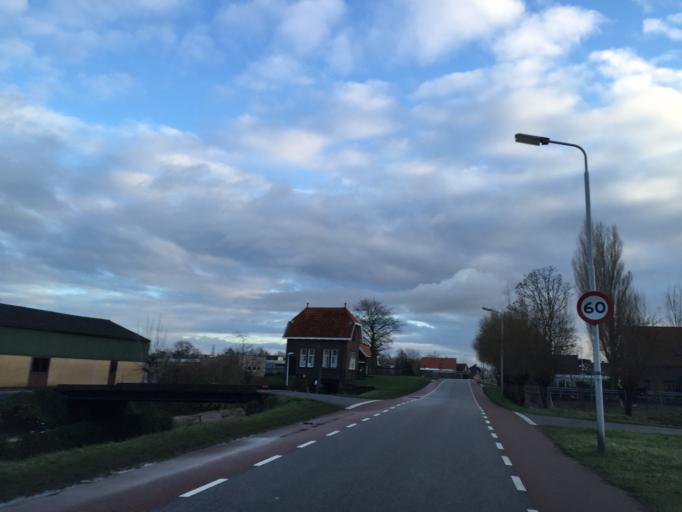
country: NL
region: South Holland
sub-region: Gemeente Pijnacker-Nootdorp
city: Pijnacker
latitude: 52.0190
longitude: 4.4200
